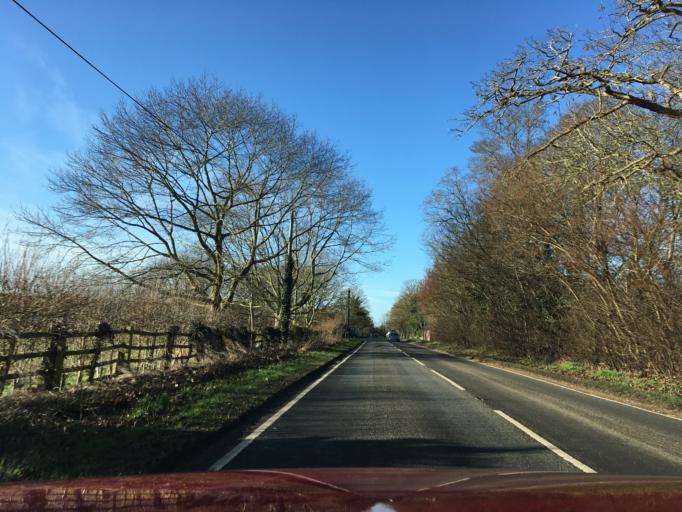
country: GB
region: England
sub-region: Warwickshire
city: Stratford-upon-Avon
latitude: 52.2029
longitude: -1.6610
